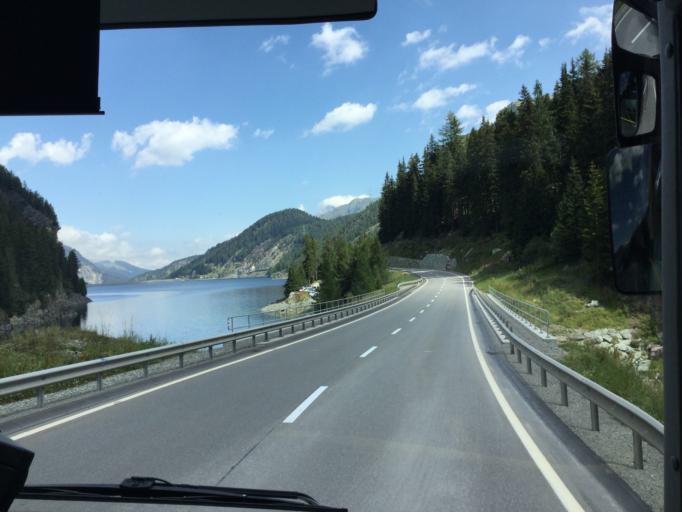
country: CH
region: Grisons
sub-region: Maloja District
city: Silvaplana
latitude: 46.4869
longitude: 9.6415
